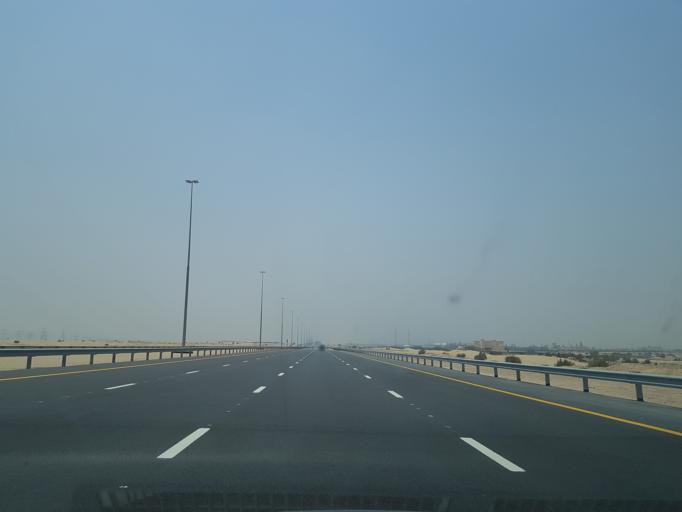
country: AE
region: Dubai
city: Dubai
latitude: 25.0738
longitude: 55.3271
